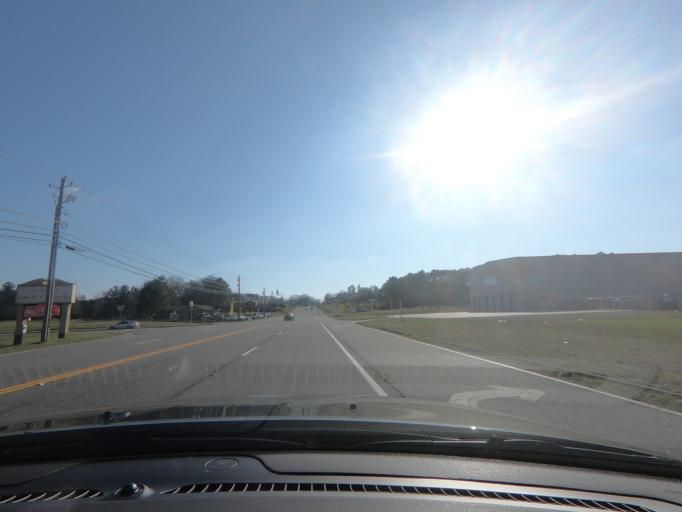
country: US
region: Georgia
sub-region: Bartow County
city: Cartersville
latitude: 34.2188
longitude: -84.7915
